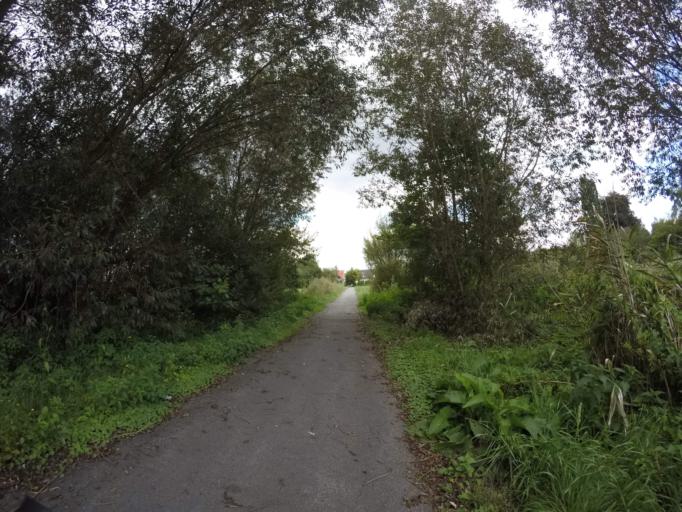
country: DE
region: North Rhine-Westphalia
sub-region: Regierungsbezirk Detmold
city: Herford
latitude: 52.1343
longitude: 8.6442
